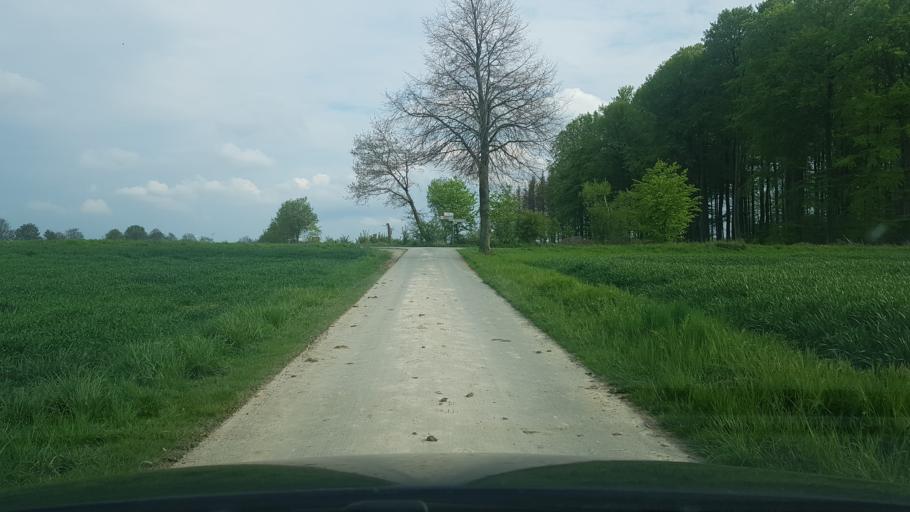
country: DE
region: North Rhine-Westphalia
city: Lichtenau
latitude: 51.6371
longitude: 8.8270
